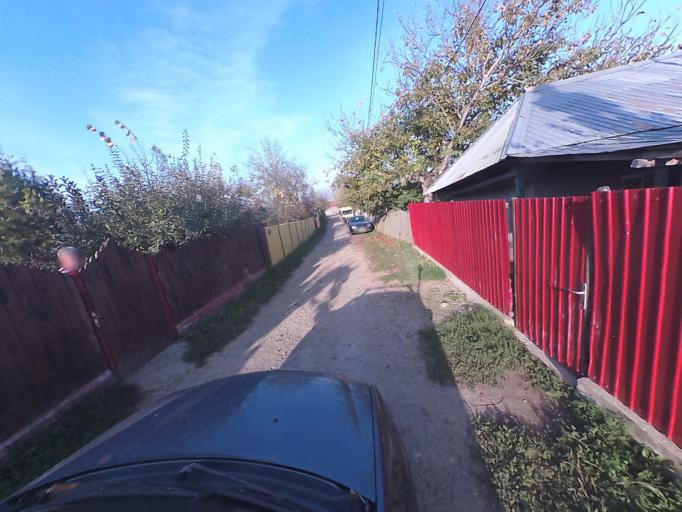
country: RO
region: Vaslui
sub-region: Comuna Bacesti
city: Bacesti
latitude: 46.8231
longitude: 27.2452
